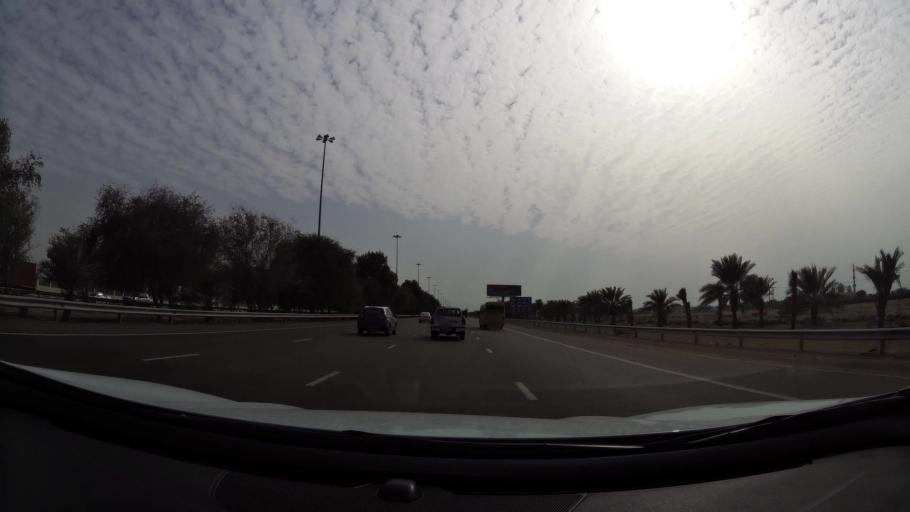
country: AE
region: Abu Dhabi
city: Abu Dhabi
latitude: 24.6140
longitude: 54.7135
